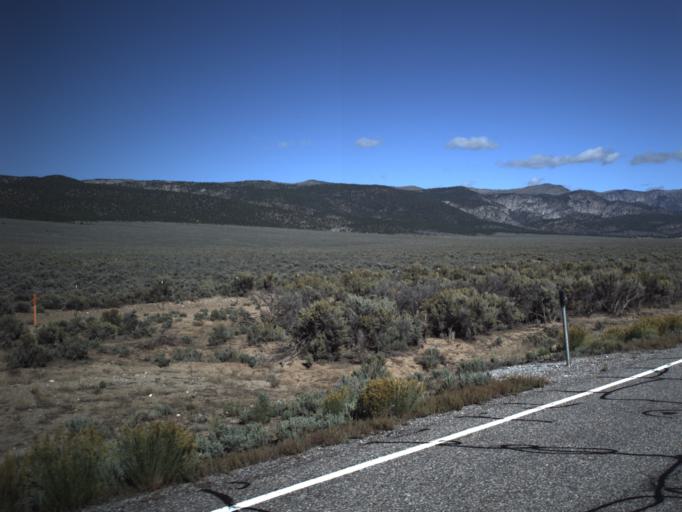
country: US
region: Utah
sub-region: Piute County
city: Junction
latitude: 38.2502
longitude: -111.9870
